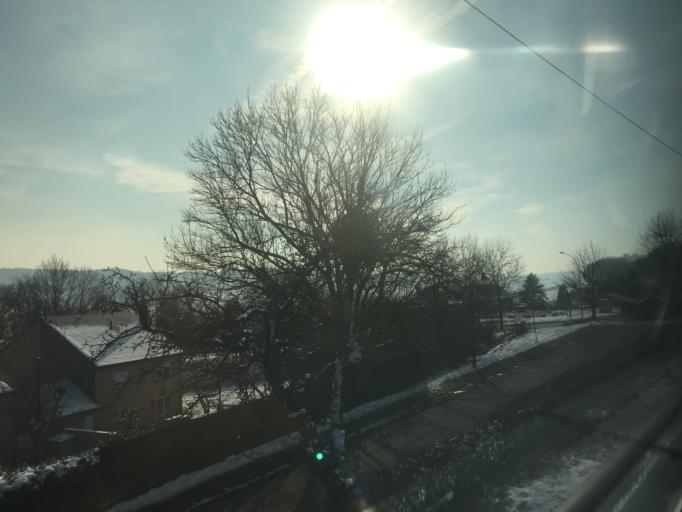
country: LU
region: Luxembourg
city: Moutfort
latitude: 49.5886
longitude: 6.2496
